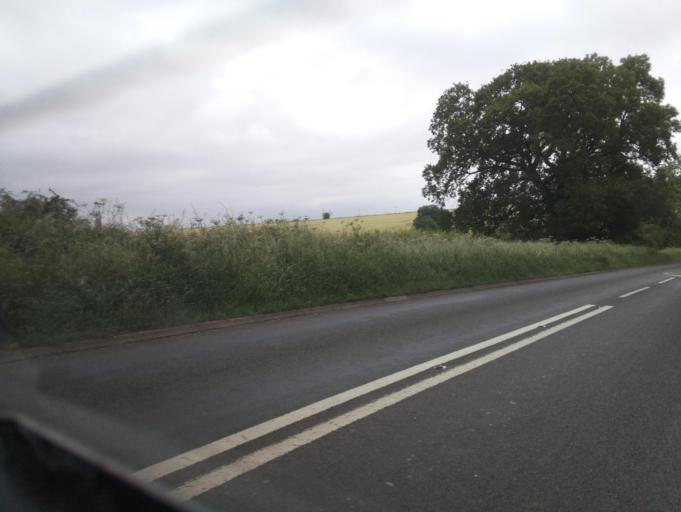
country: GB
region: England
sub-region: District of Rutland
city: Preston
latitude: 52.6055
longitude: -0.7191
